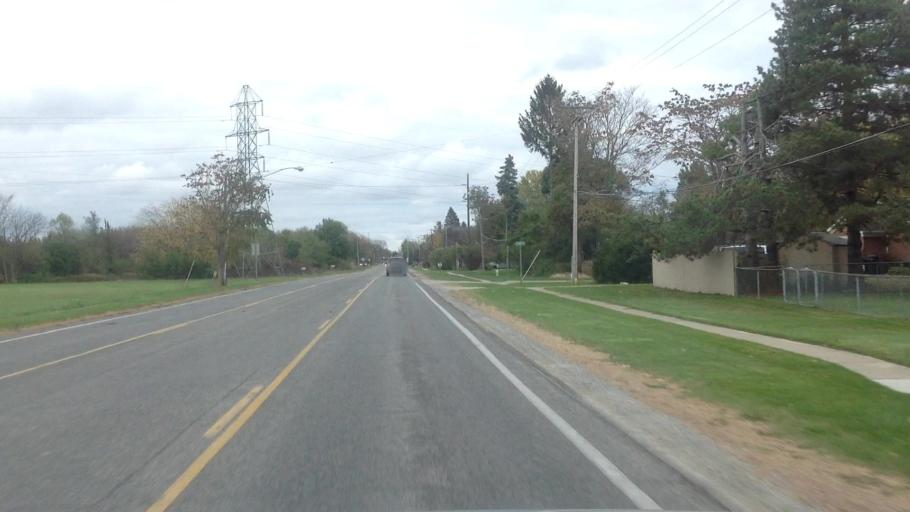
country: US
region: Michigan
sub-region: Saginaw County
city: Bridgeport
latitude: 43.3767
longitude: -83.9128
